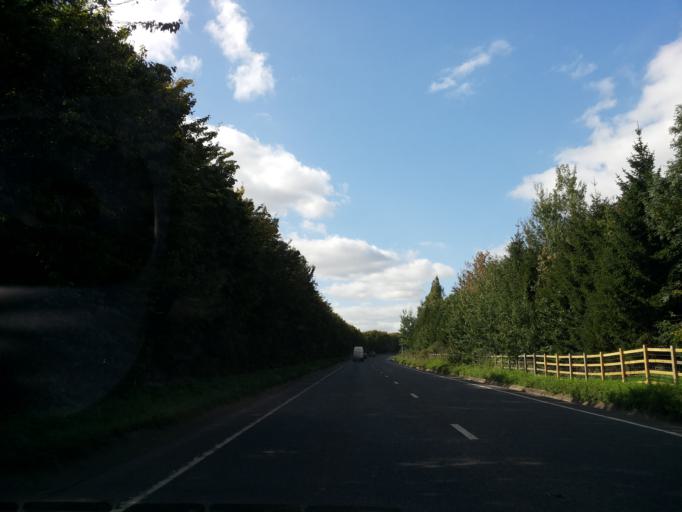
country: GB
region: England
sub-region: Wiltshire
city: Chapmanslade
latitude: 51.2562
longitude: -2.2664
